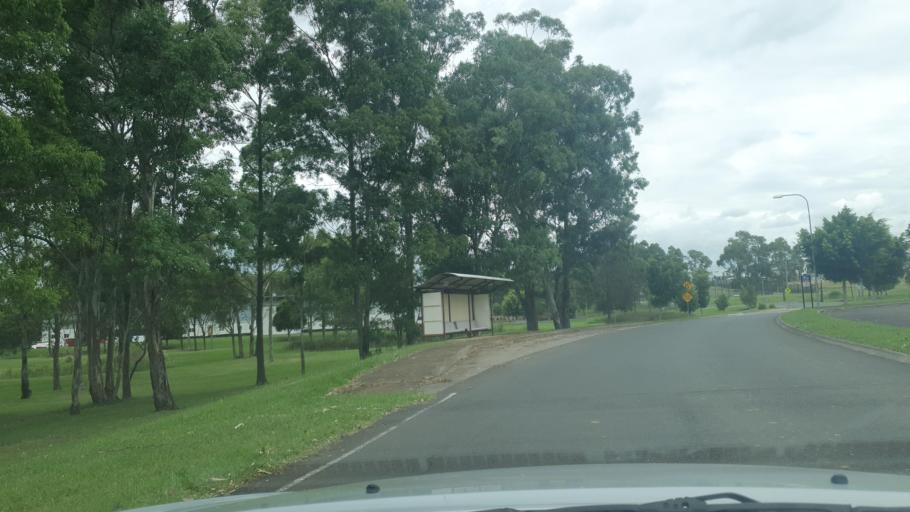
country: AU
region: New South Wales
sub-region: Penrith Municipality
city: Werrington County
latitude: -33.7697
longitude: 150.7433
